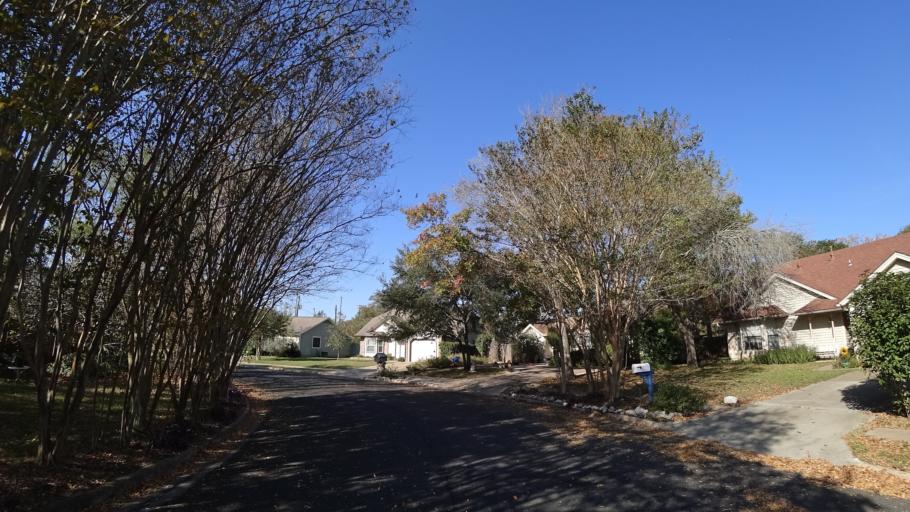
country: US
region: Texas
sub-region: Travis County
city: Barton Creek
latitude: 30.2335
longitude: -97.8534
